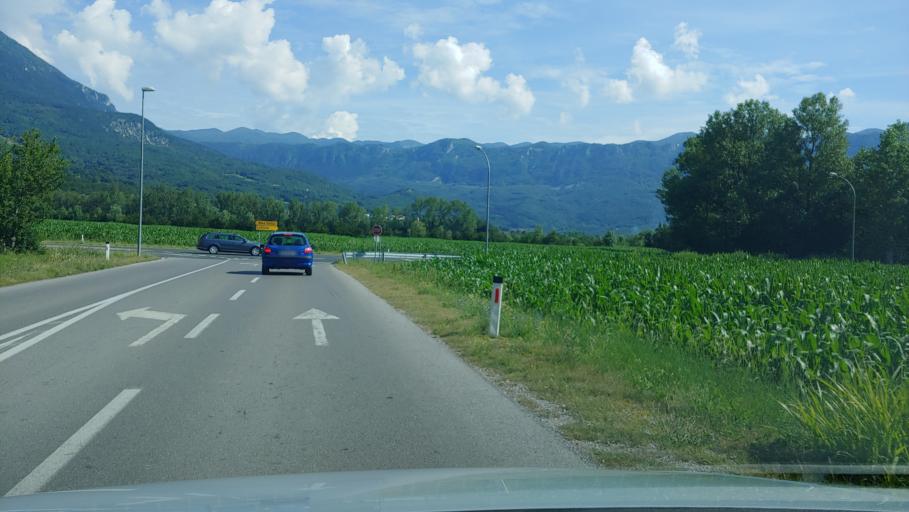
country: SI
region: Ajdovscina
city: Lokavec
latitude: 45.8862
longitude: 13.8760
